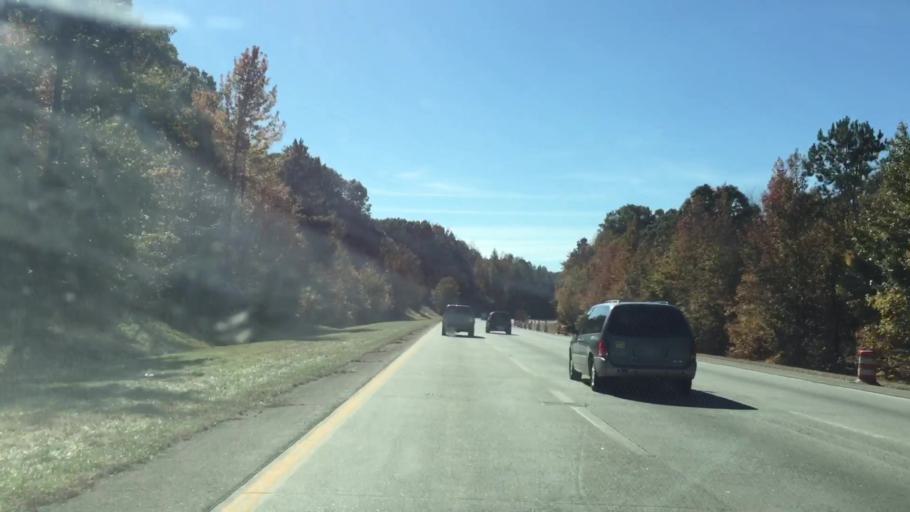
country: US
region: North Carolina
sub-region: Davidson County
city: Thomasville
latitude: 35.8307
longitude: -80.1484
